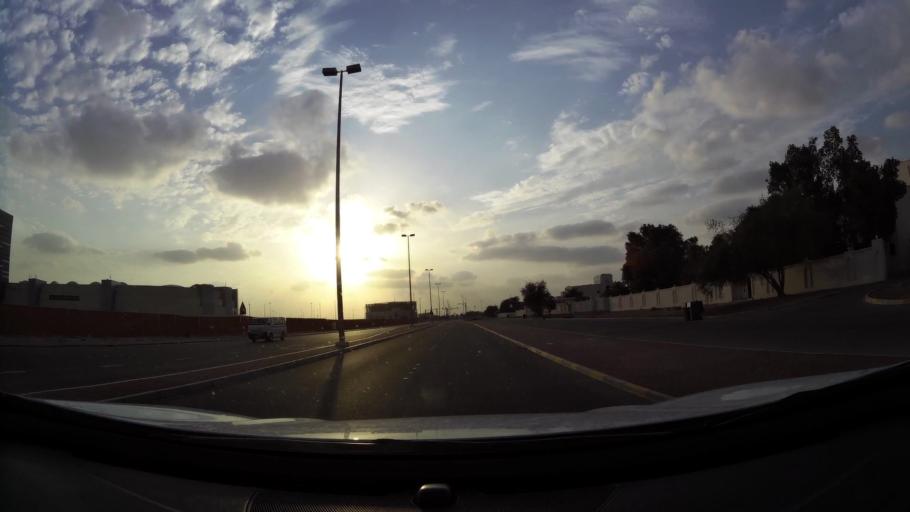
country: AE
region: Abu Dhabi
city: Abu Dhabi
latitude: 24.3788
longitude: 54.5330
